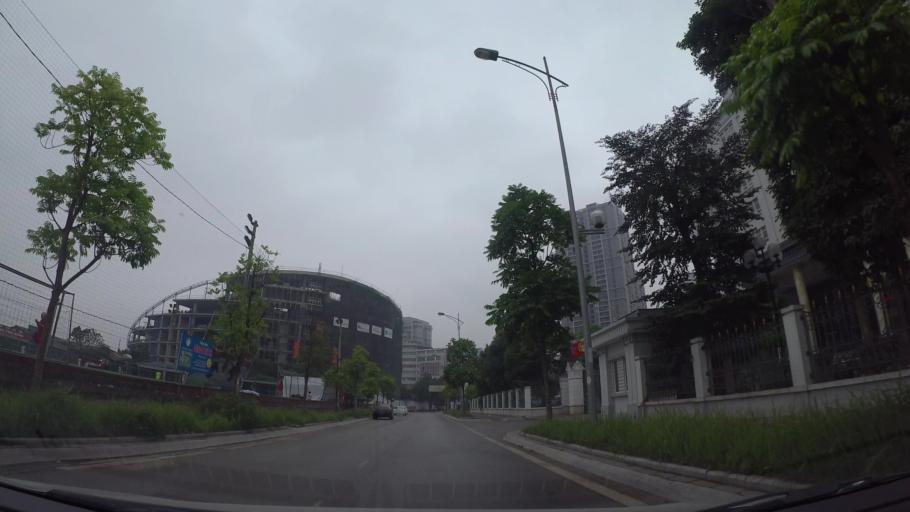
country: VN
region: Ha Noi
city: Cau Giay
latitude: 21.0244
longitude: 105.7869
